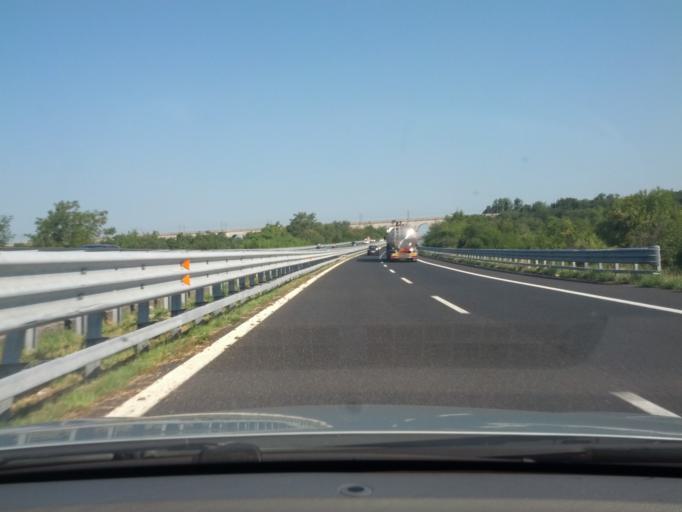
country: IT
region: Friuli Venezia Giulia
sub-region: Provincia di Trieste
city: Aurisina
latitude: 45.7519
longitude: 13.6768
